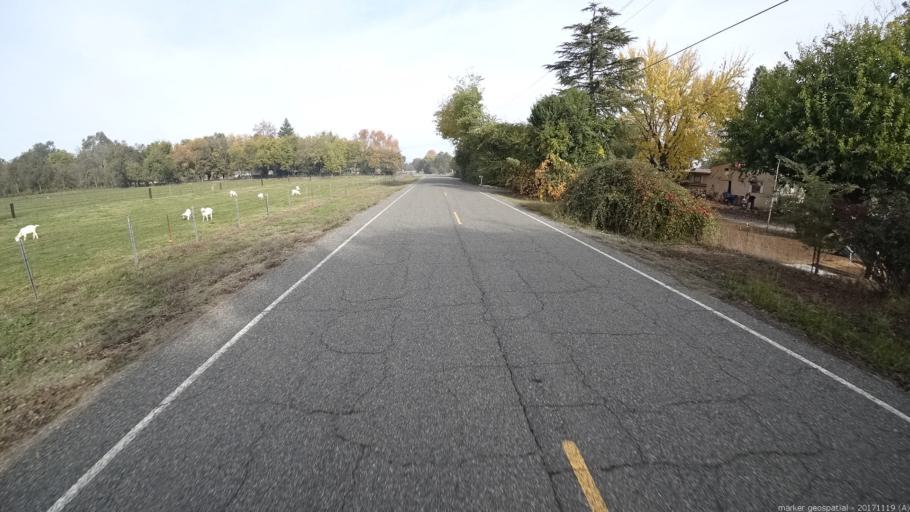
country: US
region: California
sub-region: Shasta County
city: Redding
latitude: 40.5163
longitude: -122.3491
